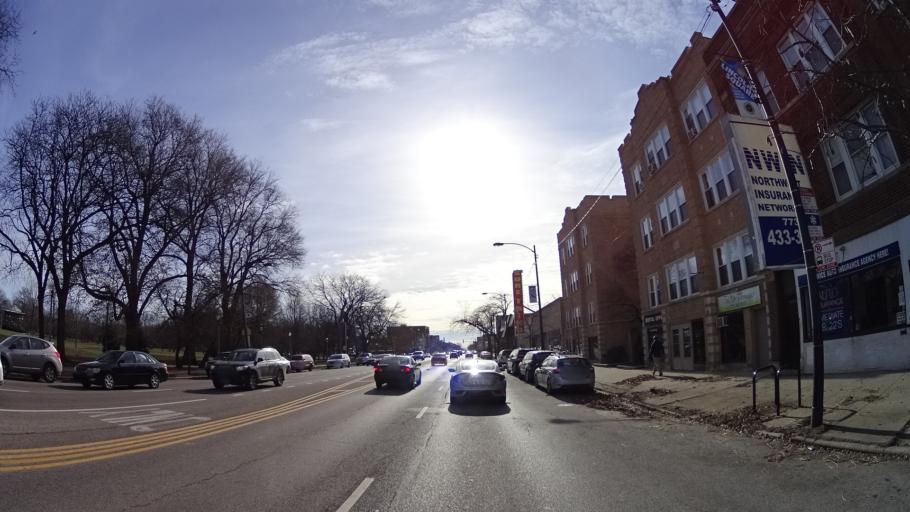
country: US
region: Illinois
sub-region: Cook County
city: Lincolnwood
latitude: 41.9629
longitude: -87.6888
